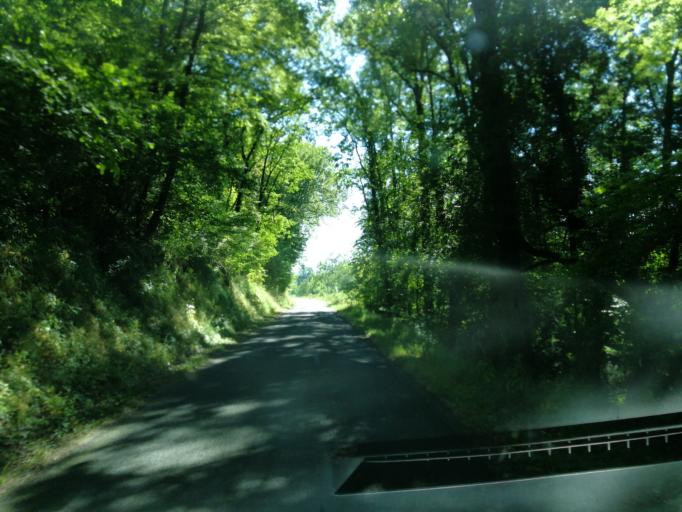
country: FR
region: Aquitaine
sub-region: Departement de la Dordogne
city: Eyvigues-et-Eybenes
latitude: 44.8746
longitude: 1.3868
